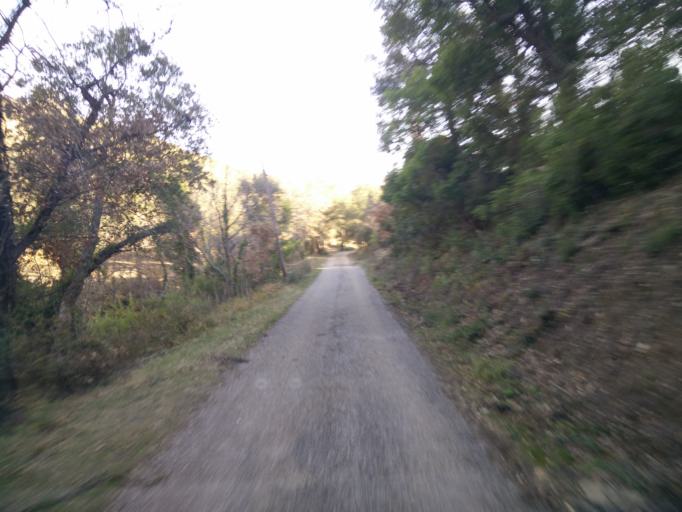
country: FR
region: Provence-Alpes-Cote d'Azur
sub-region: Departement du Var
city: Collobrieres
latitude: 43.2541
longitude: 6.3077
